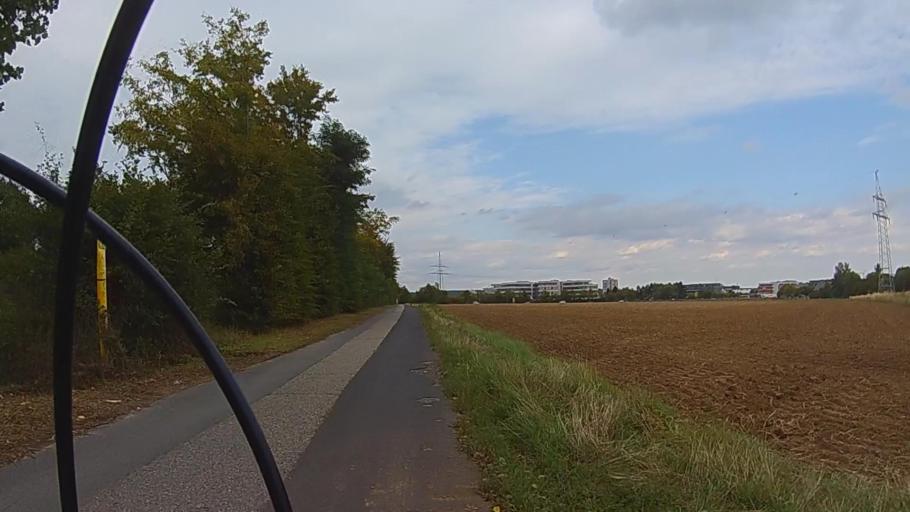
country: DE
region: Hesse
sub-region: Regierungsbezirk Darmstadt
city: Bad Homburg vor der Hoehe
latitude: 50.2082
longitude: 8.6077
